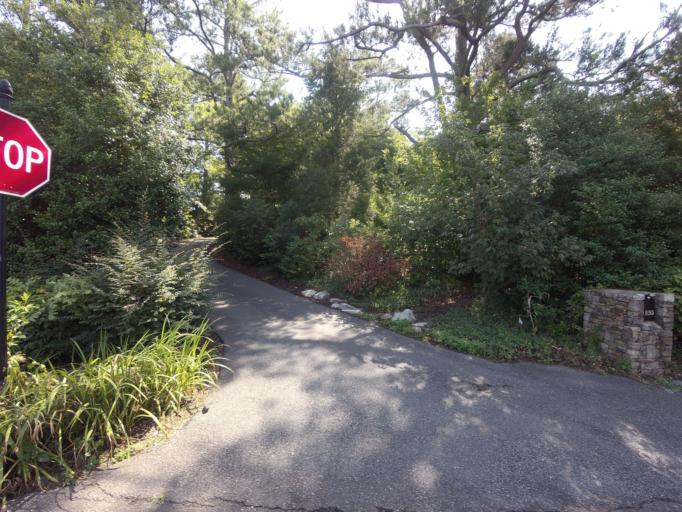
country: US
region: Georgia
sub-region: Fulton County
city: Johns Creek
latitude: 34.0698
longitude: -84.2152
